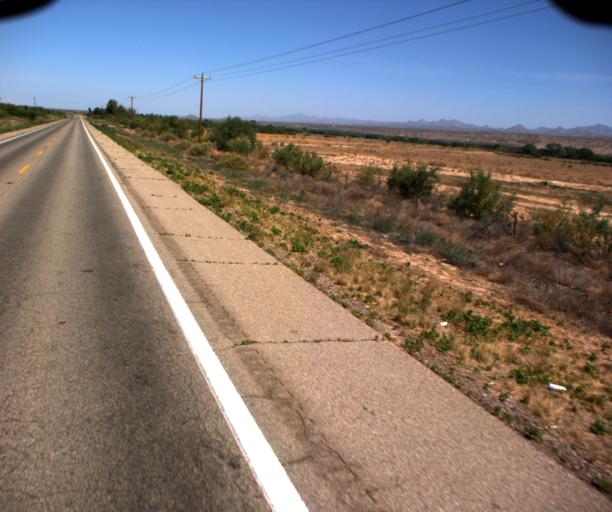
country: US
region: Arizona
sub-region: Graham County
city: Bylas
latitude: 33.0624
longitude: -110.0069
